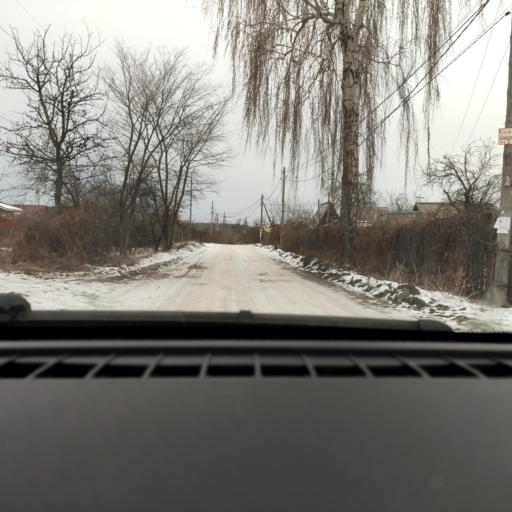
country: RU
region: Voronezj
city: Maslovka
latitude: 51.6027
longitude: 39.2850
